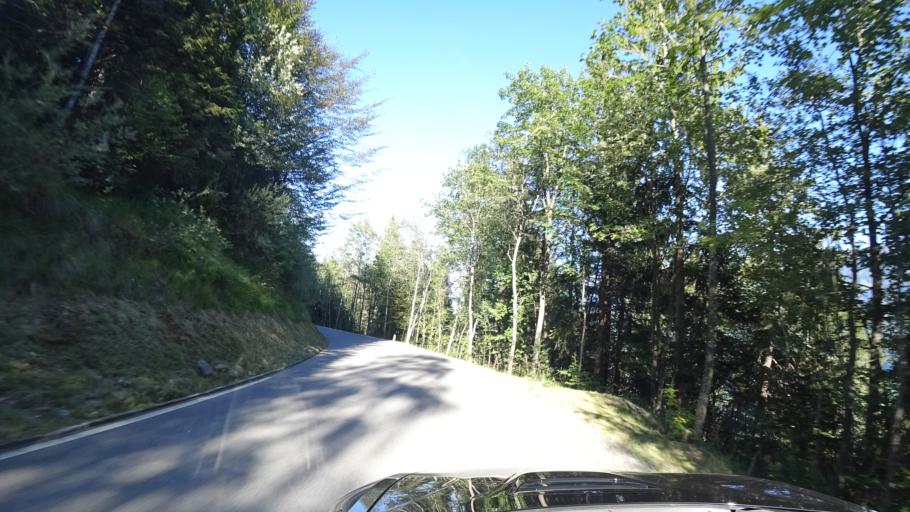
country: CH
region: Obwalden
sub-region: Obwalden
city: Giswil
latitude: 46.8310
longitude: 8.1338
